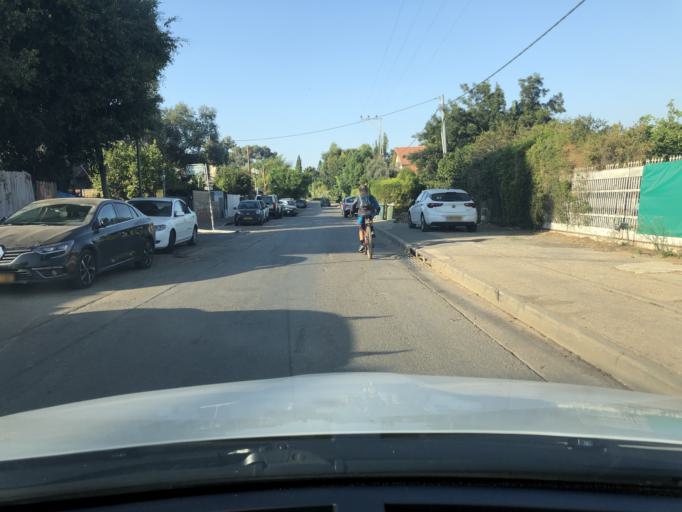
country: IL
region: Central District
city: Hod HaSharon
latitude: 32.1395
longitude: 34.9032
